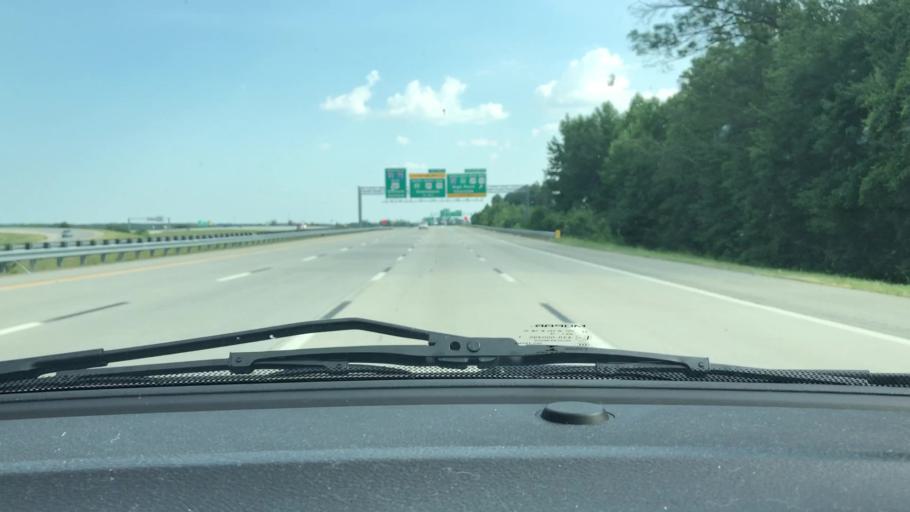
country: US
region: North Carolina
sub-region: Guilford County
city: Jamestown
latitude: 36.0120
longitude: -79.8533
